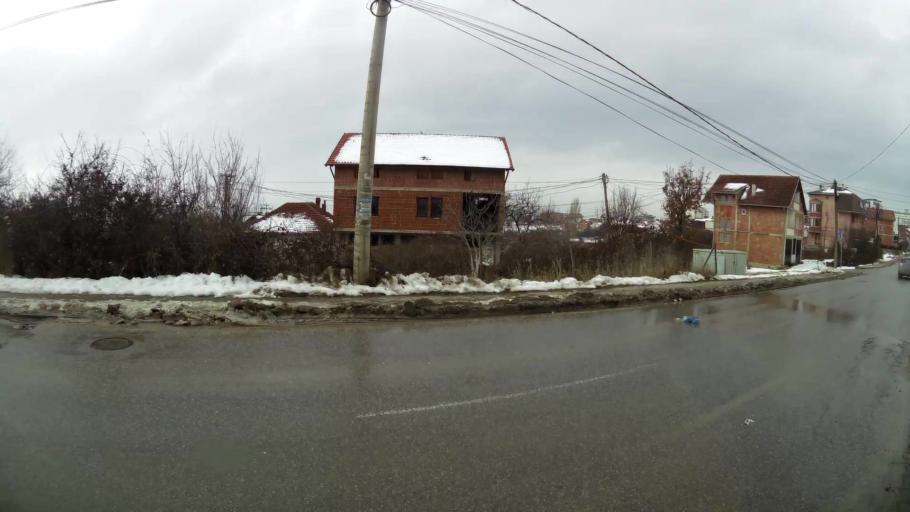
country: XK
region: Pristina
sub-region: Komuna e Prishtines
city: Pristina
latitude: 42.6500
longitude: 21.1940
